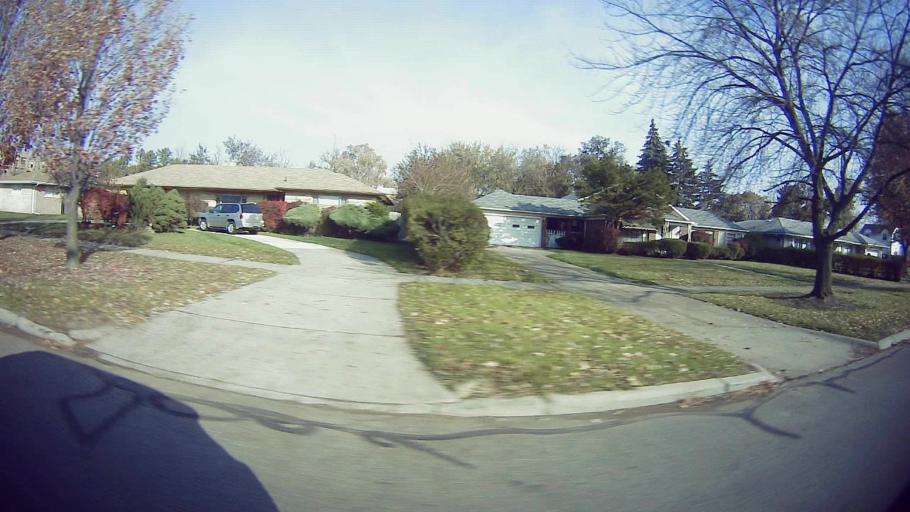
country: US
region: Michigan
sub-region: Wayne County
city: Highland Park
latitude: 42.4195
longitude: -83.1177
